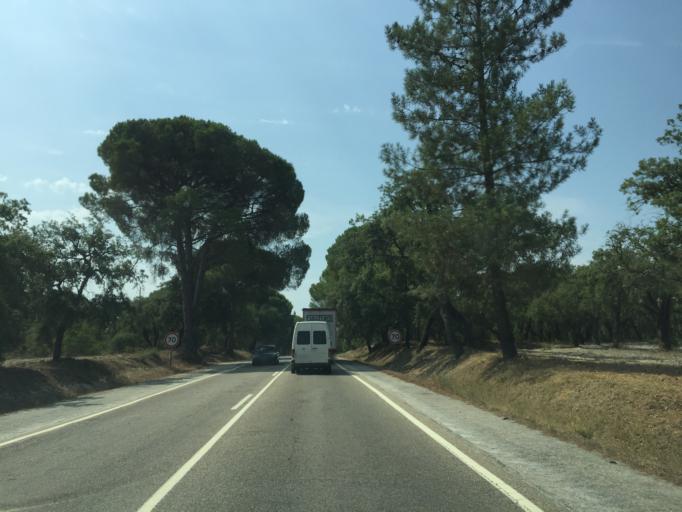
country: PT
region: Setubal
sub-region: Alcacer do Sal
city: Alcacer do Sal
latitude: 38.3006
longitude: -8.5324
